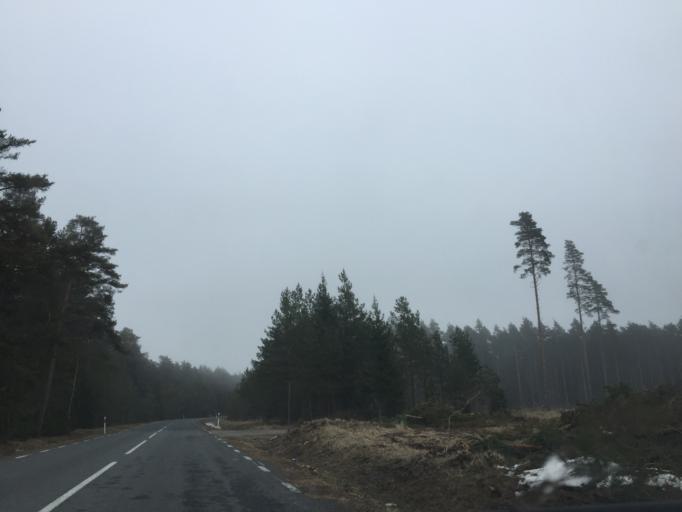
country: EE
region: Saare
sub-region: Kuressaare linn
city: Kuressaare
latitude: 58.4683
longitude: 22.0239
